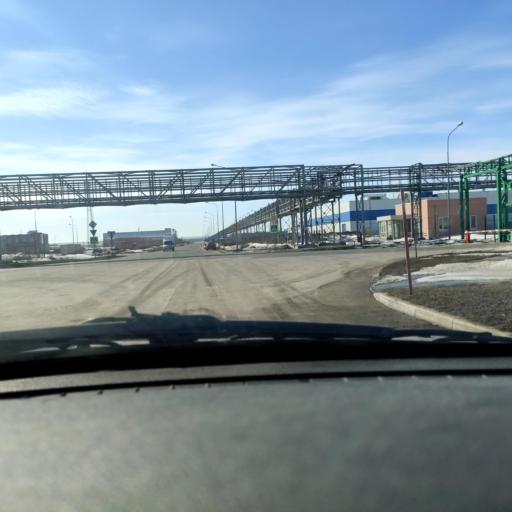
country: RU
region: Samara
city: Podstepki
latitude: 53.5602
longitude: 49.1844
